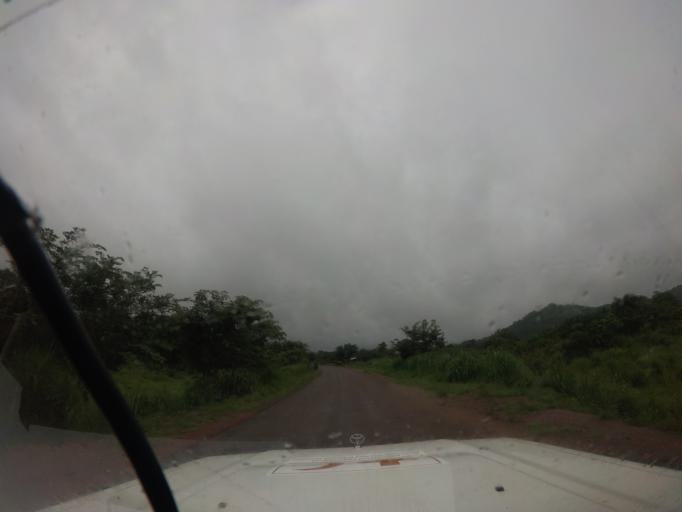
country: SL
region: Northern Province
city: Bumbuna
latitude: 9.3257
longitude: -11.8662
